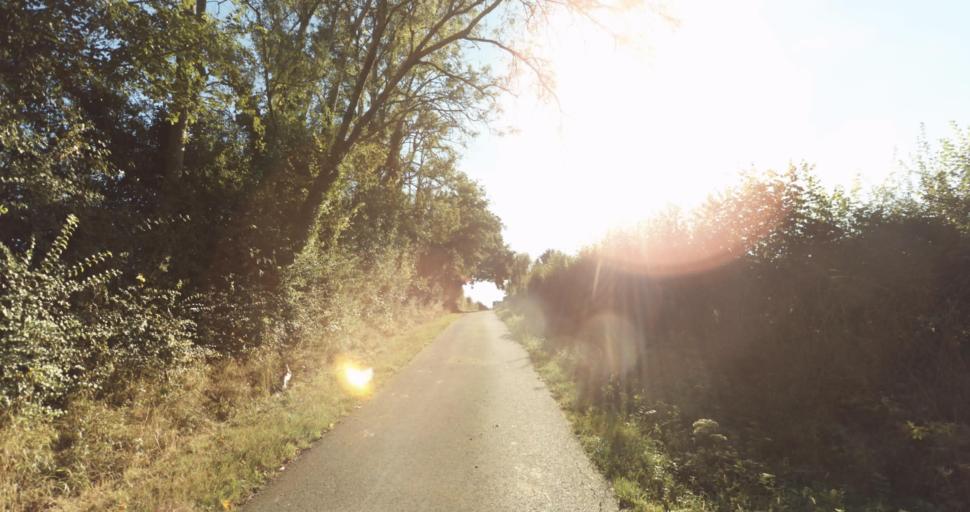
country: FR
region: Lower Normandy
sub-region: Departement de l'Orne
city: Vimoutiers
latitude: 48.8825
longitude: 0.1258
